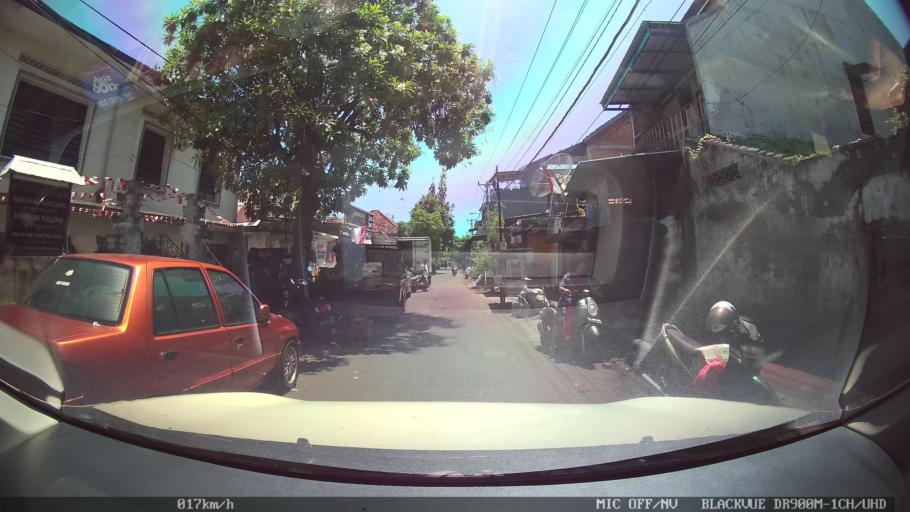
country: ID
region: Bali
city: Banjar Kampunganyar
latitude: -8.1089
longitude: 115.0884
